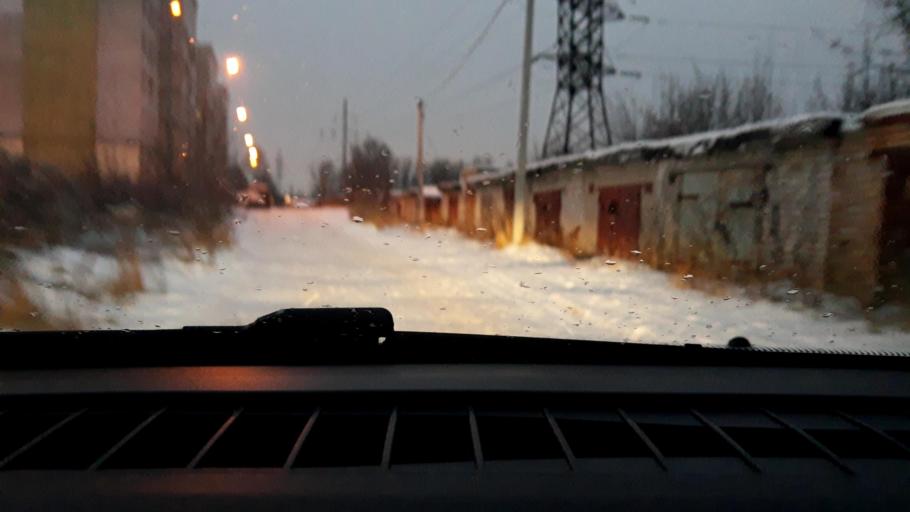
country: RU
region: Nizjnij Novgorod
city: Gorbatovka
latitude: 56.2942
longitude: 43.8600
